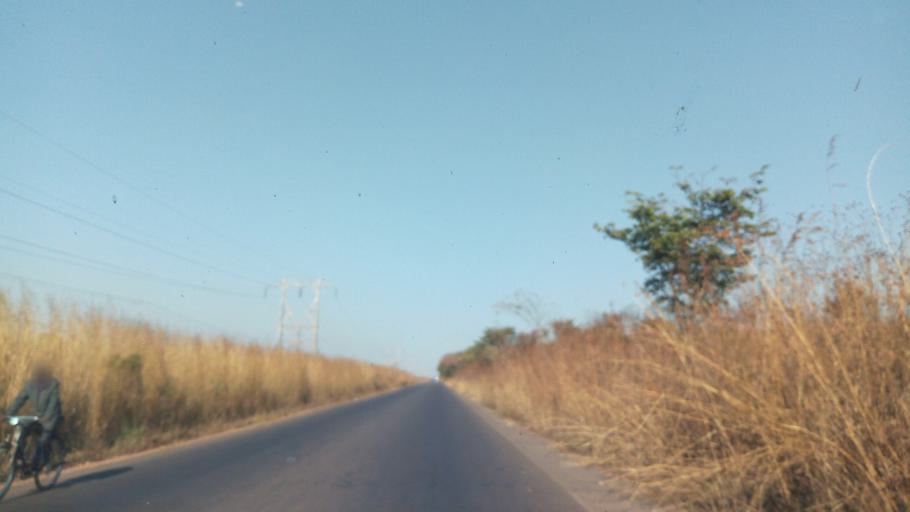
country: CD
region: Katanga
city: Likasi
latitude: -11.0033
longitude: 26.8986
